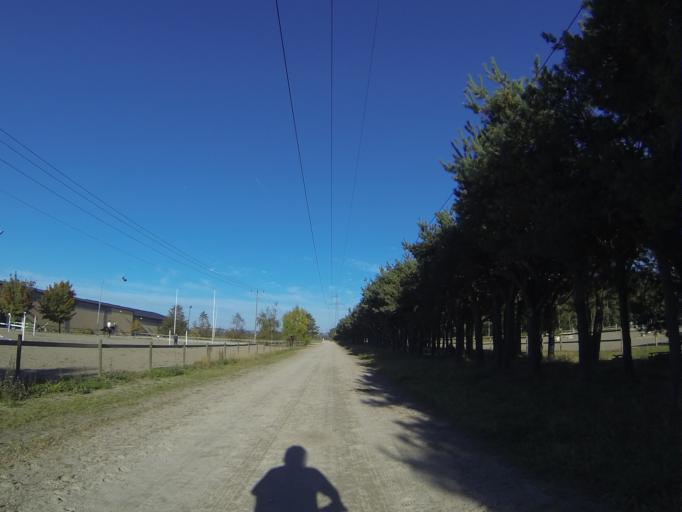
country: SE
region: Skane
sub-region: Eslovs Kommun
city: Eslov
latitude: 55.7348
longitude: 13.3604
